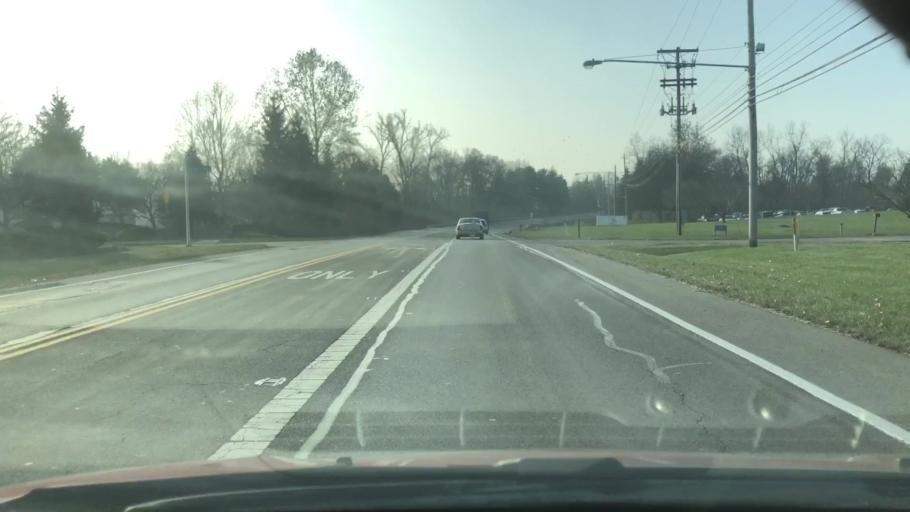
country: US
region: Ohio
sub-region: Franklin County
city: Minerva Park
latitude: 40.0725
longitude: -82.9288
